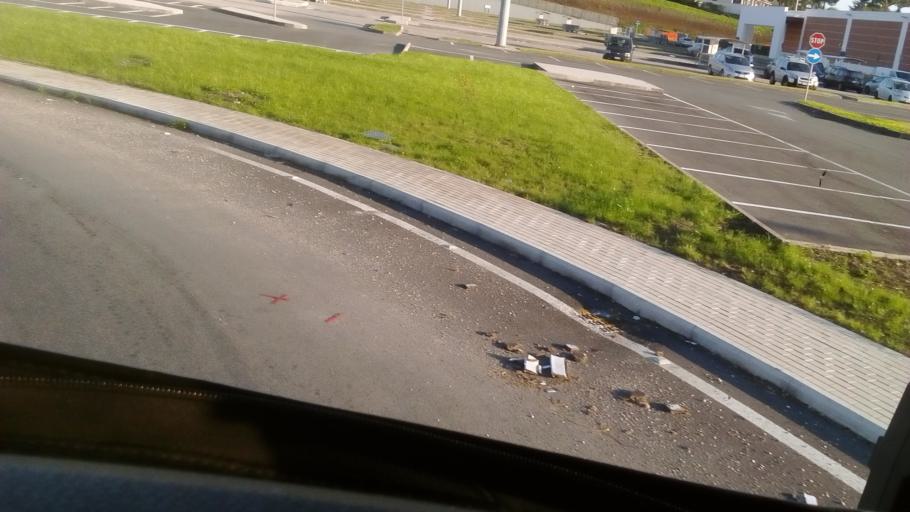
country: IT
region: Latium
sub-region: Citta metropolitana di Roma Capitale
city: Pavona
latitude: 41.7180
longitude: 12.6234
